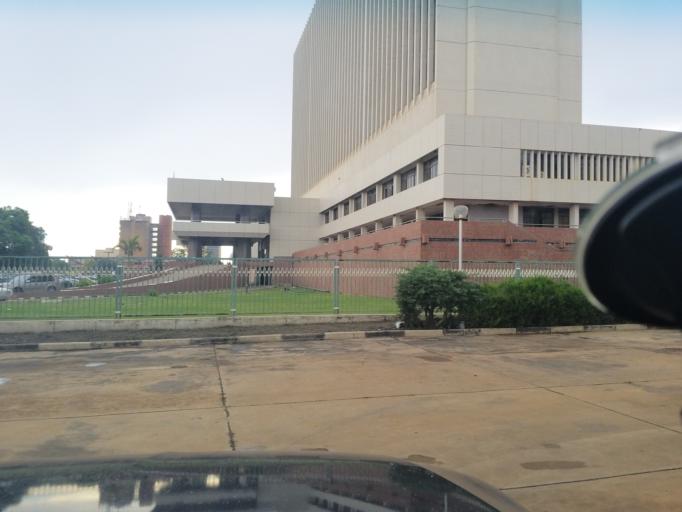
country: ZM
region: Lusaka
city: Lusaka
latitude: -15.4224
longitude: 28.2912
